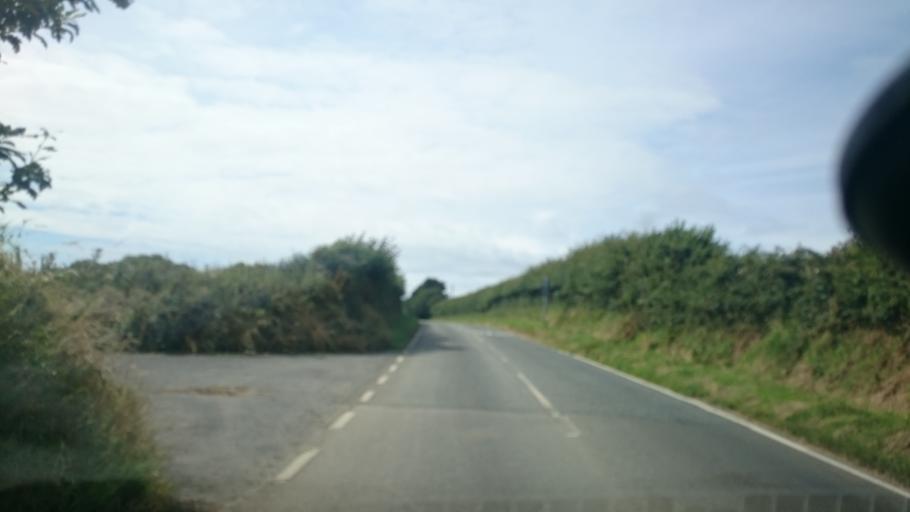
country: GB
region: Wales
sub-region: Pembrokeshire
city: Llangwm
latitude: 51.7509
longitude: -4.9191
